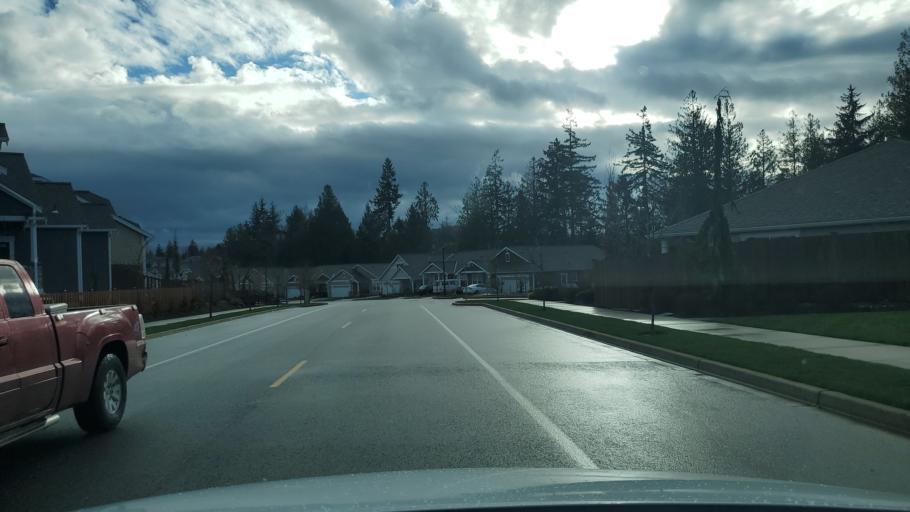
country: US
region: Washington
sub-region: Skagit County
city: Big Lake
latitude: 48.4195
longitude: -122.2792
